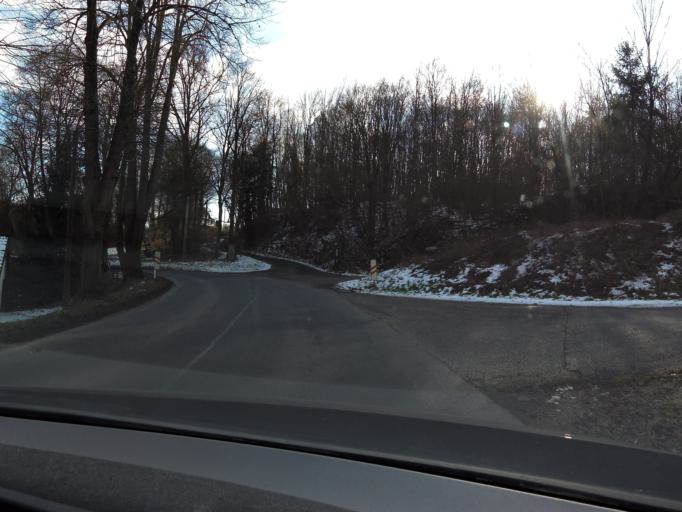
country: DE
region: Thuringia
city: Leimbach
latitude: 50.8429
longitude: 10.2052
